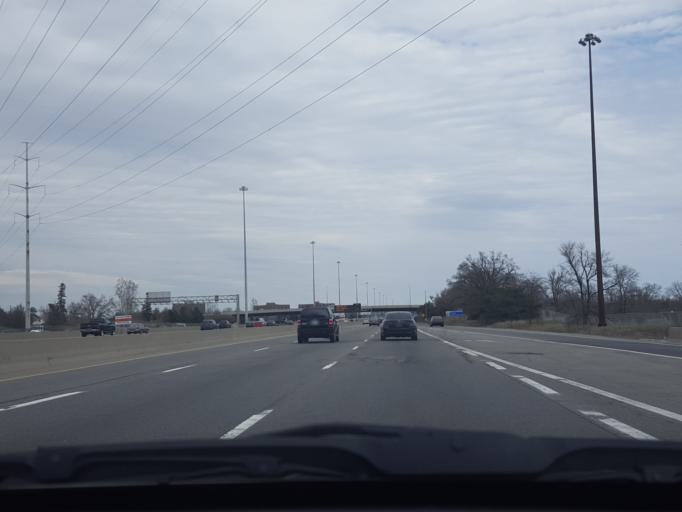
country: CA
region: Ontario
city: Scarborough
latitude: 43.7967
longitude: -79.1929
